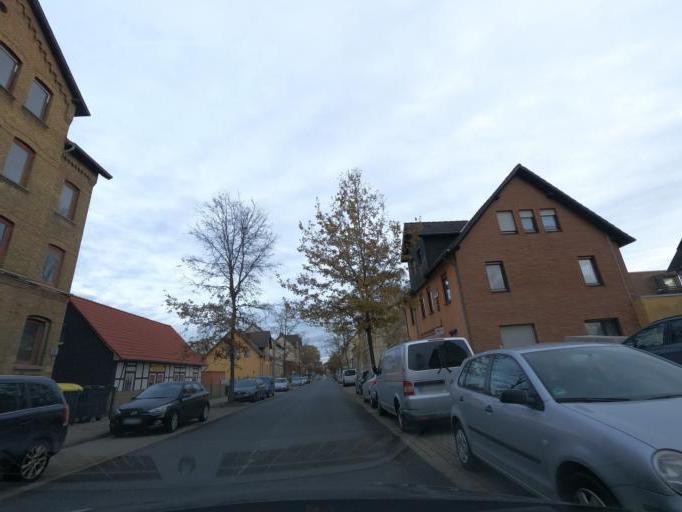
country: DE
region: Lower Saxony
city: Braunschweig
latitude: 52.2605
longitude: 10.4920
